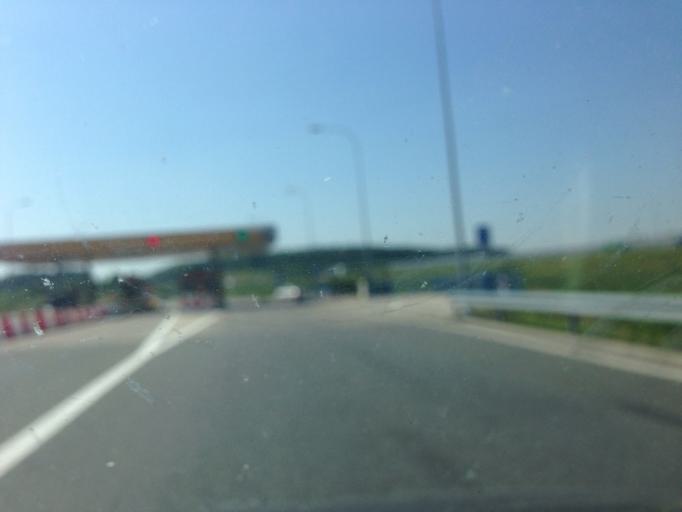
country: PL
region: Pomeranian Voivodeship
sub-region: Powiat tczewski
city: Pelplin
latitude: 53.9308
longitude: 18.6432
